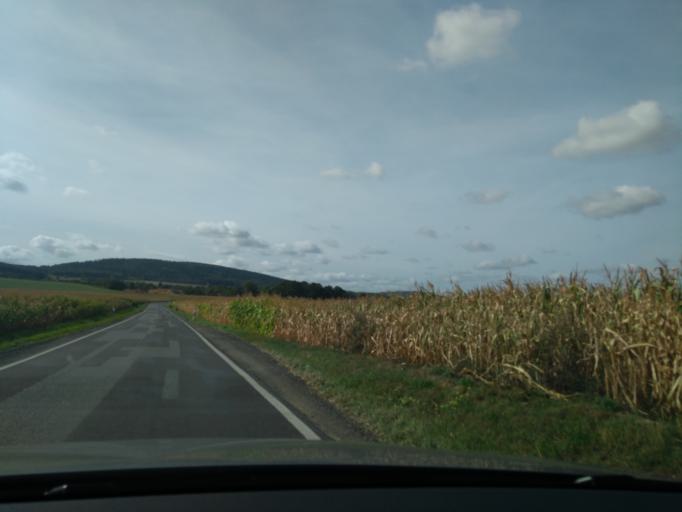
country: DE
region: Saxony
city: Kubschutz
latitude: 51.1585
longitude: 14.4652
